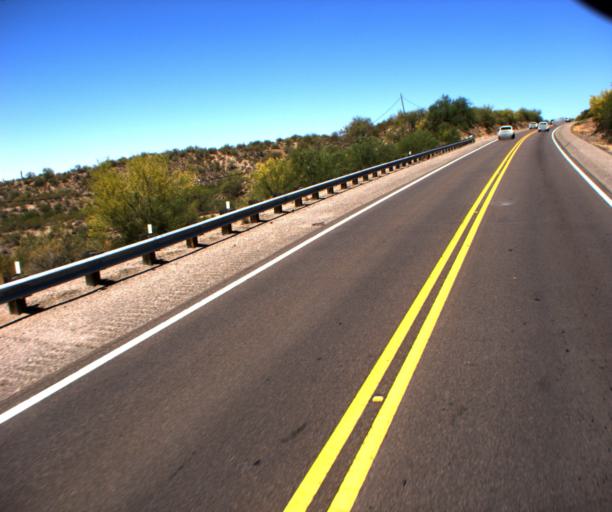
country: US
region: Arizona
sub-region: Maricopa County
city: Wickenburg
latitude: 33.9938
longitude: -112.7531
